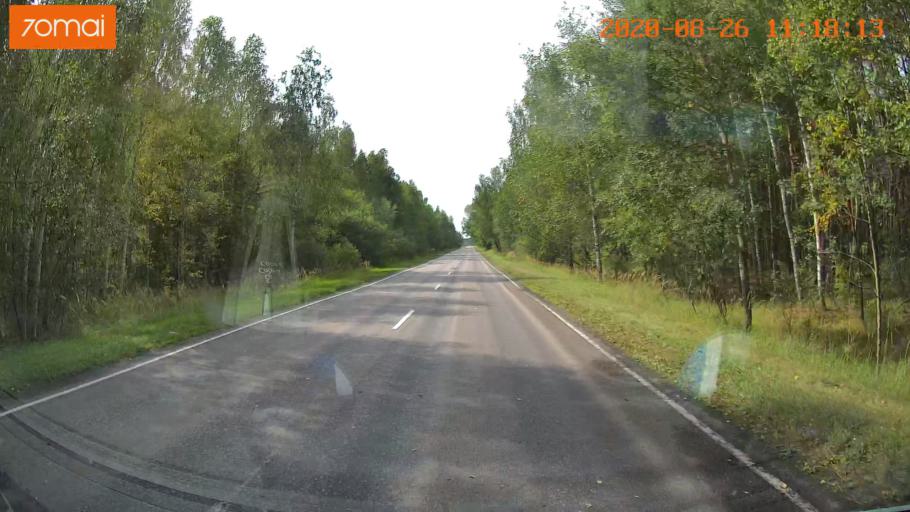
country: RU
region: Rjazan
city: Shilovo
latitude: 54.4121
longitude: 41.1009
